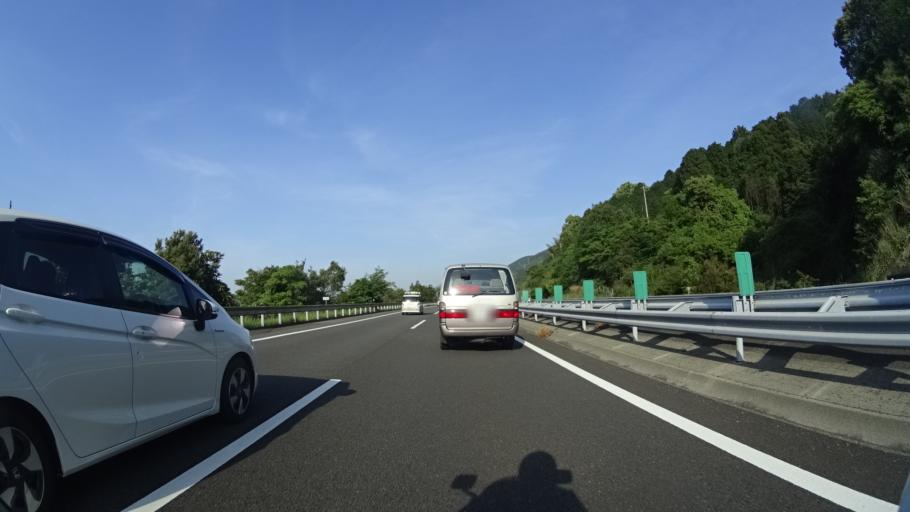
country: JP
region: Ehime
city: Kawanoecho
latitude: 33.9604
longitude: 133.4998
